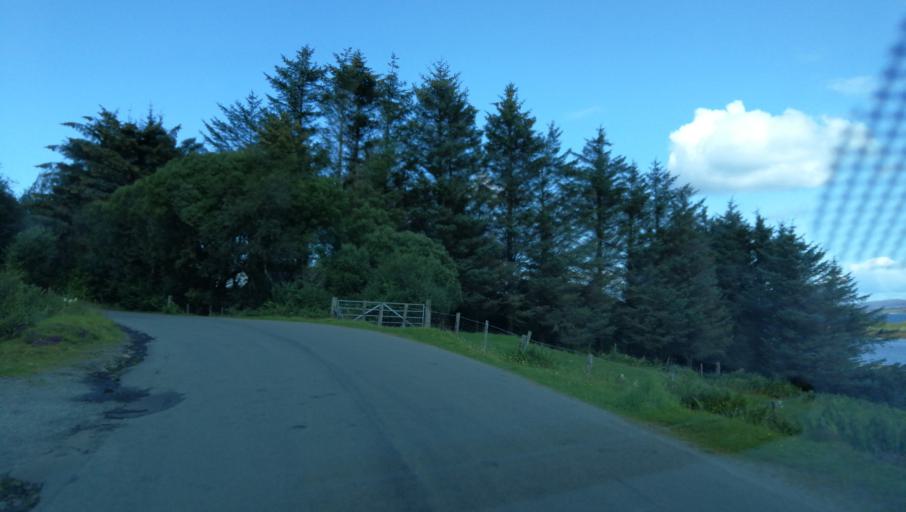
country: GB
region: Scotland
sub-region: Highland
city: Isle of Skye
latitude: 57.4474
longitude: -6.6462
